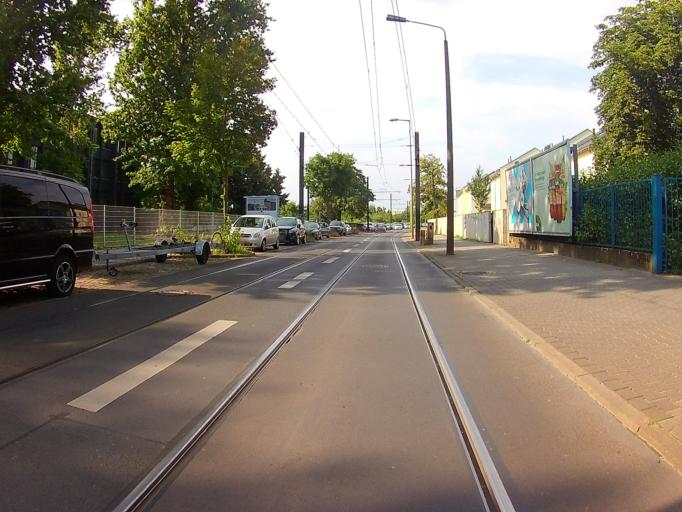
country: DE
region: Berlin
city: Kopenick Bezirk
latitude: 52.4313
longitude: 13.5716
